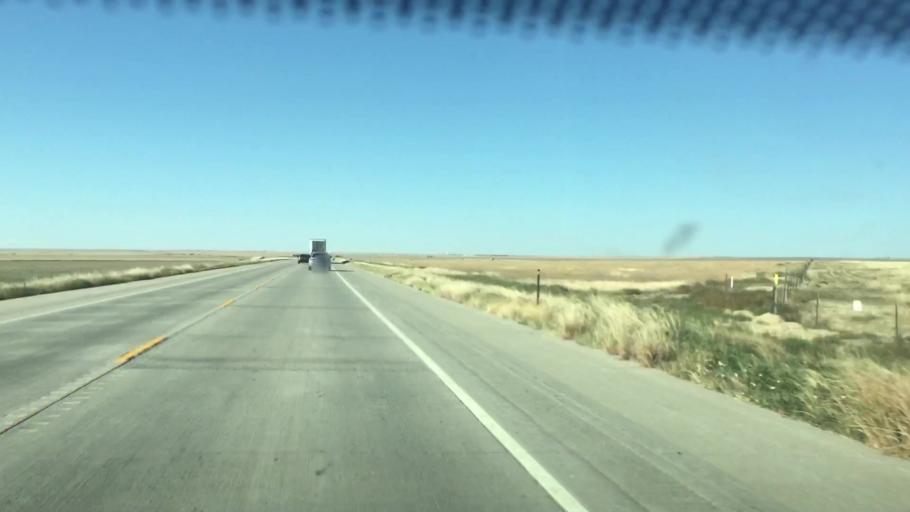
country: US
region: Colorado
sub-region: Kiowa County
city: Eads
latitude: 38.3616
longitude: -102.7207
